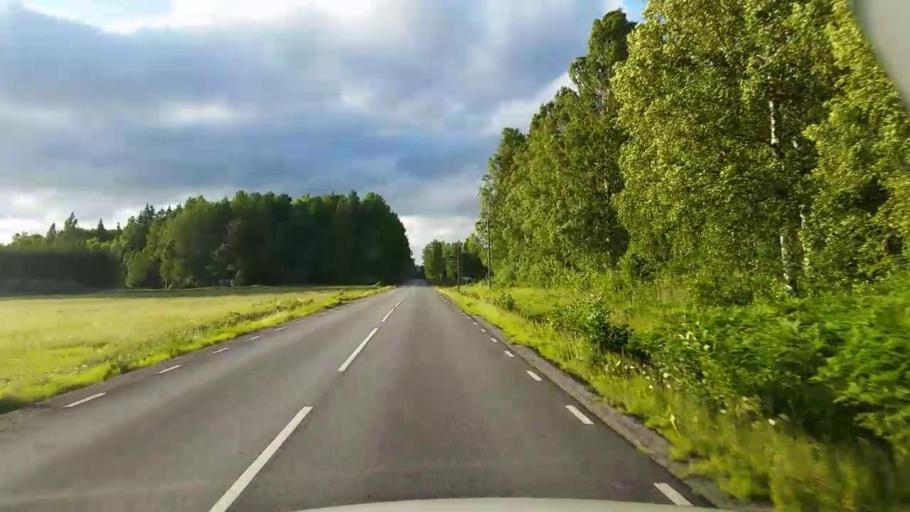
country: SE
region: Vaestmanland
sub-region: Kopings Kommun
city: Kolsva
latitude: 59.7094
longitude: 15.8289
